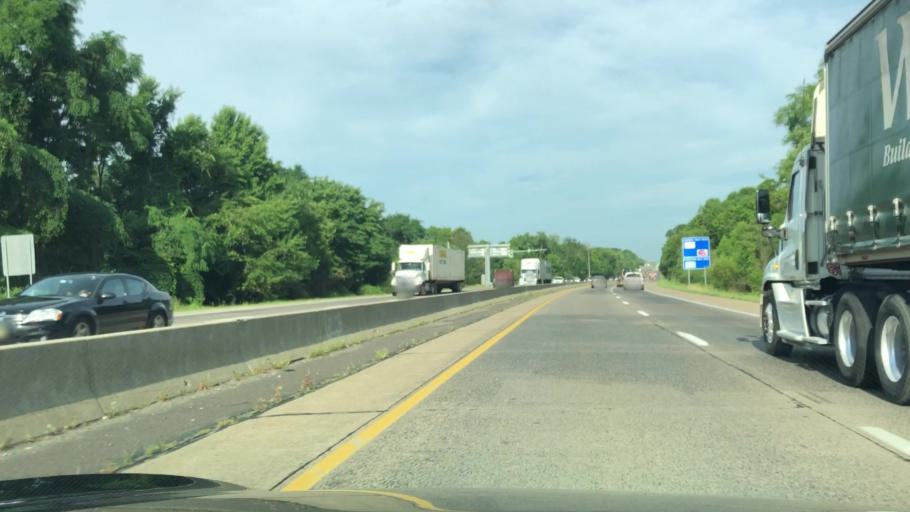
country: US
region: Pennsylvania
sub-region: Bucks County
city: Fairless Hills
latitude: 40.1940
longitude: -74.8438
